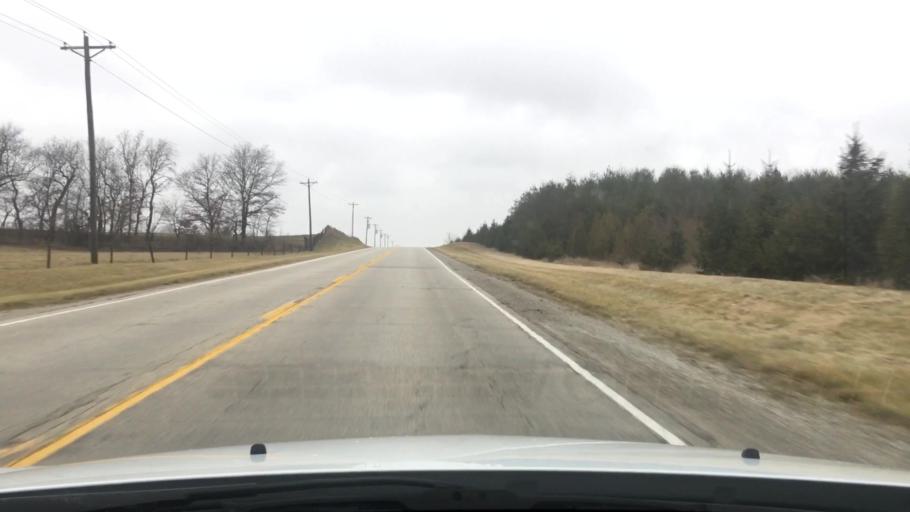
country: US
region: Illinois
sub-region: Iroquois County
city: Watseka
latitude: 40.8907
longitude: -87.6863
